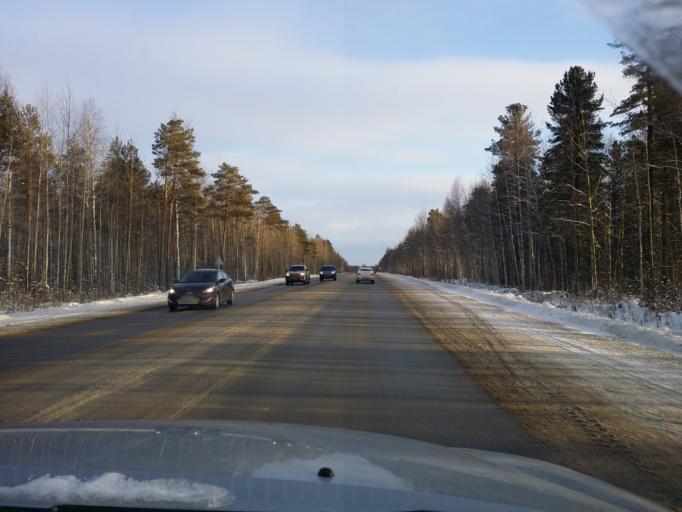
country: RU
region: Khanty-Mansiyskiy Avtonomnyy Okrug
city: Megion
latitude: 61.0571
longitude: 76.2980
